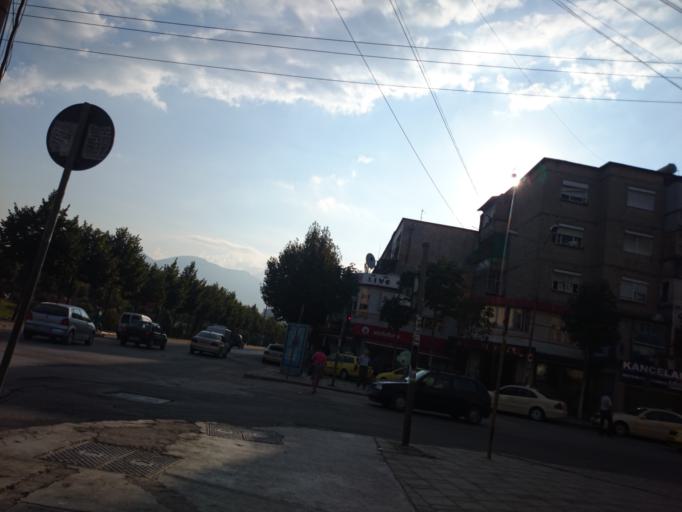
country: AL
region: Tirane
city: Tirana
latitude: 41.3203
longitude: 19.7990
